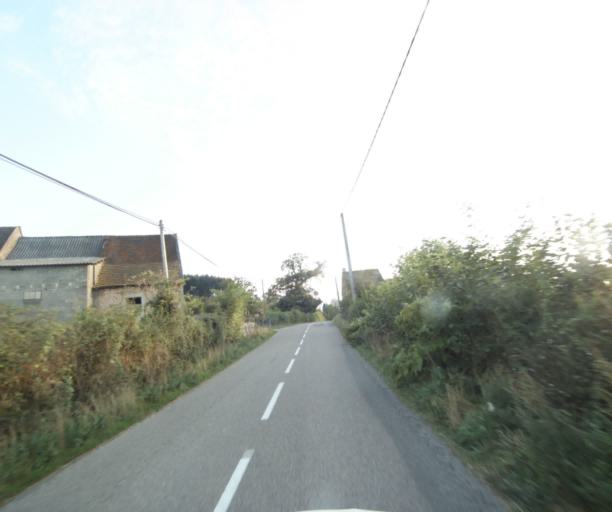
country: FR
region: Bourgogne
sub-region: Departement de Saone-et-Loire
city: Charolles
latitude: 46.4091
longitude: 4.4022
